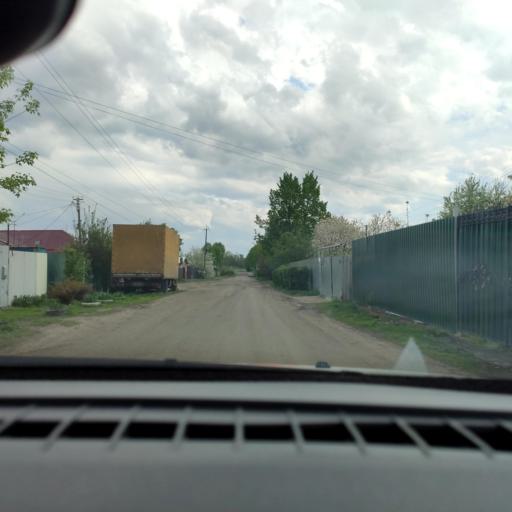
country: RU
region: Voronezj
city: Maslovka
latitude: 51.5355
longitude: 39.3369
